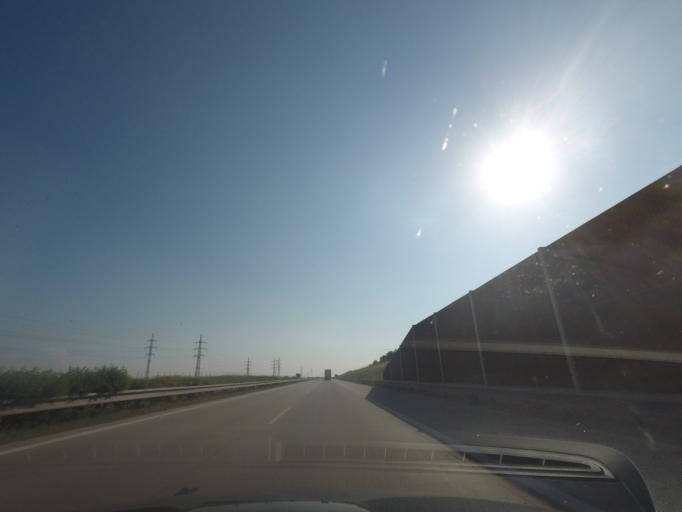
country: CZ
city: Jesenik nad Odrou
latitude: 49.6600
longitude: 17.9041
